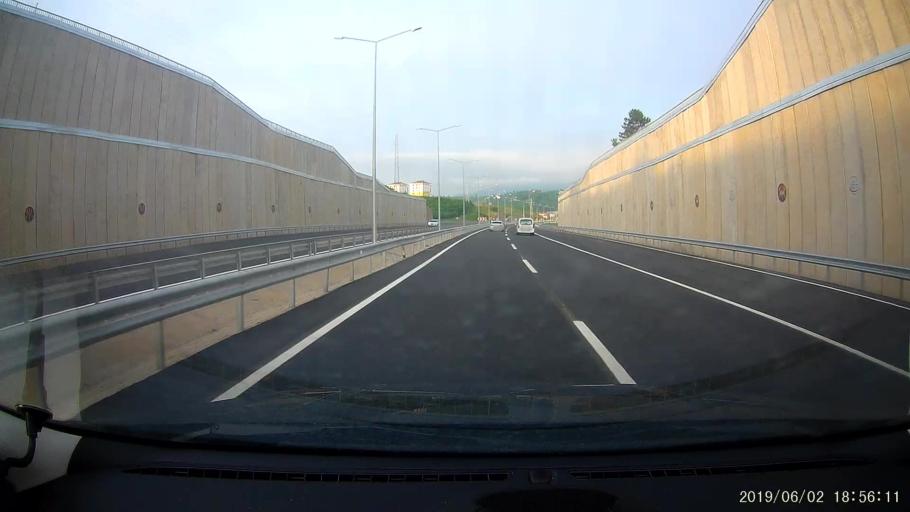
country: TR
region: Ordu
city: Ordu
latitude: 40.9561
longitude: 37.8856
